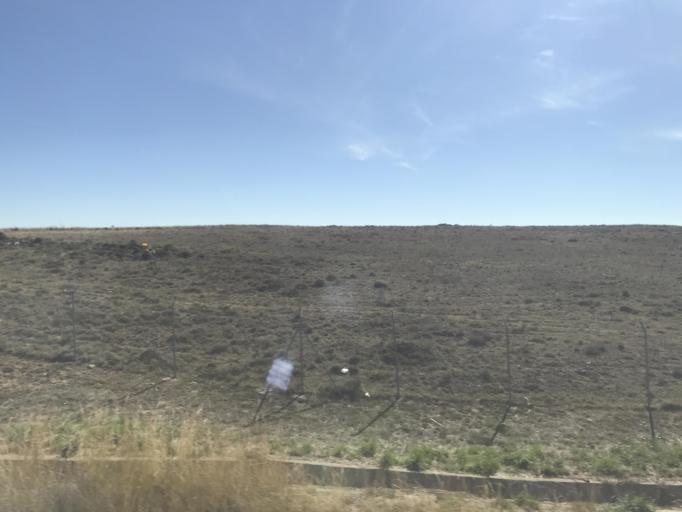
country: ES
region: Castille-La Mancha
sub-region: Provincia de Guadalajara
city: Anguita
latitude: 41.1129
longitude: -2.3598
